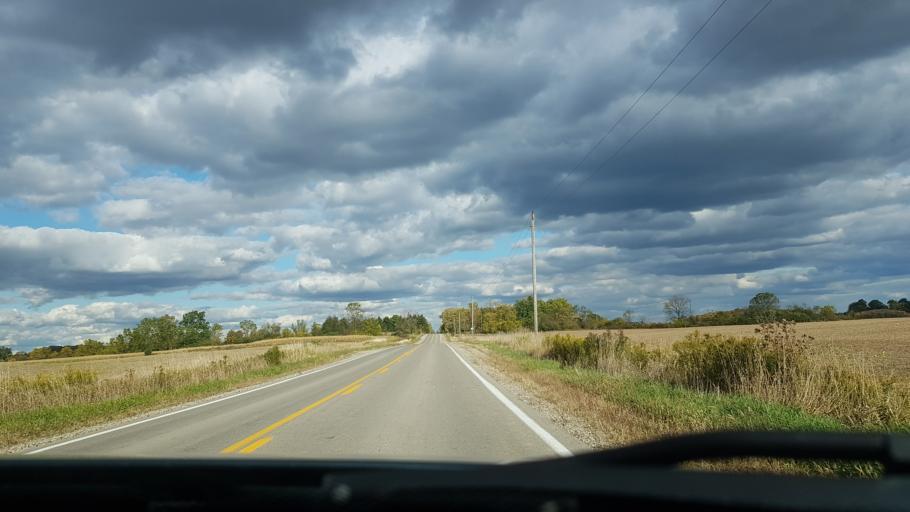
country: CA
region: Ontario
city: Delaware
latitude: 43.0188
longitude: -81.3553
